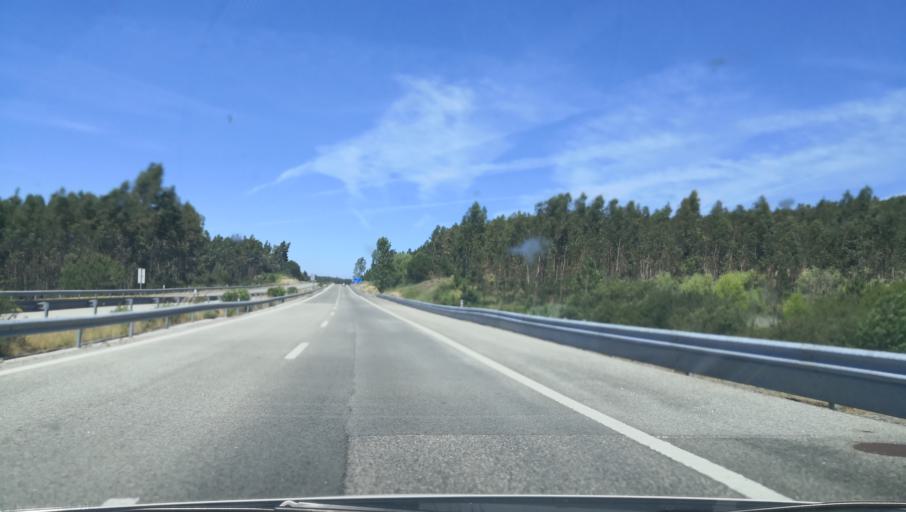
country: PT
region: Coimbra
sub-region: Montemor-O-Velho
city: Montemor-o-Velho
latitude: 40.1762
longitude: -8.7076
